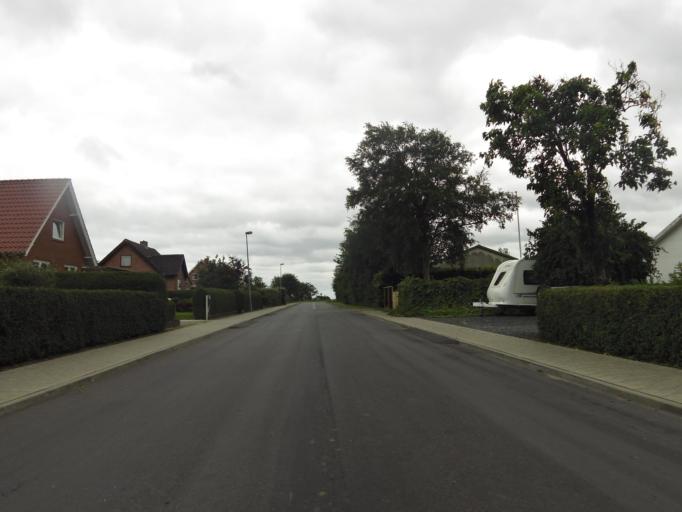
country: DK
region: South Denmark
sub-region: Tonder Kommune
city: Toftlund
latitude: 55.2536
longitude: 9.1580
